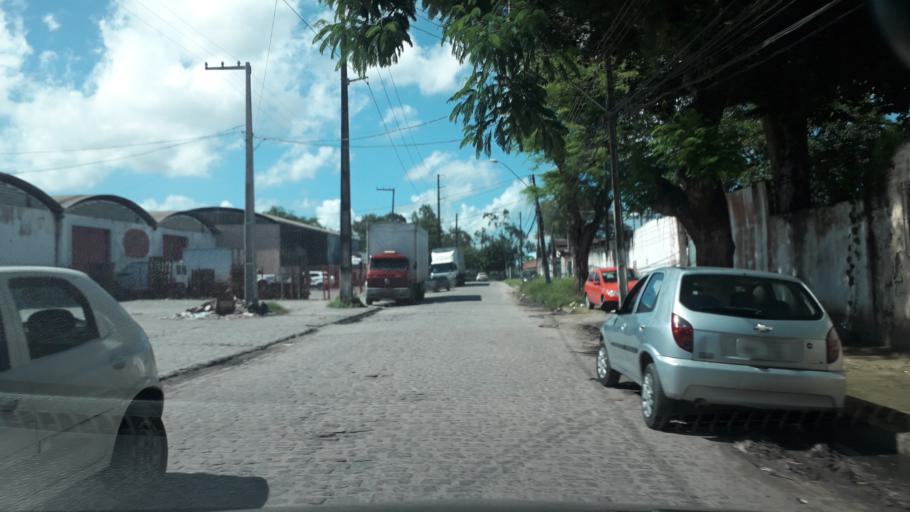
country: BR
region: Alagoas
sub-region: Satuba
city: Satuba
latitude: -9.5825
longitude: -35.7677
